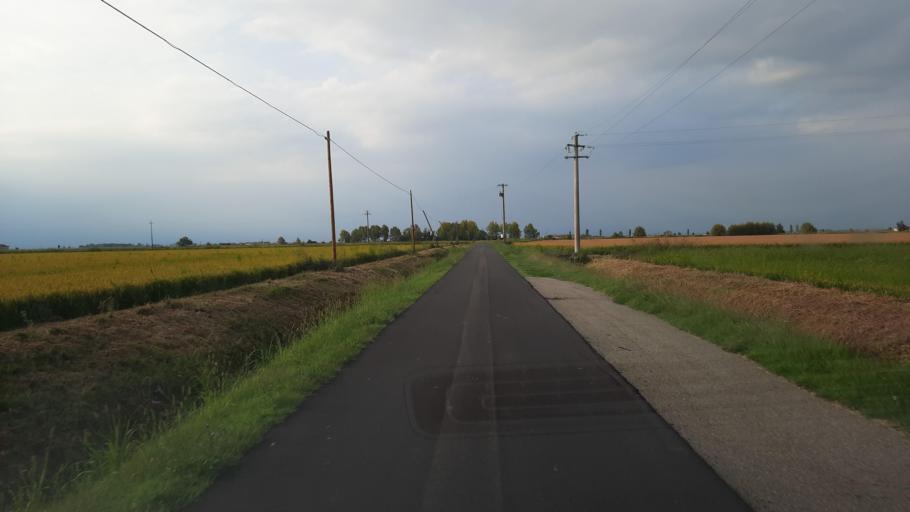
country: IT
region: Piedmont
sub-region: Provincia di Vercelli
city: Sali Vercellese
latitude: 45.3198
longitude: 8.3479
